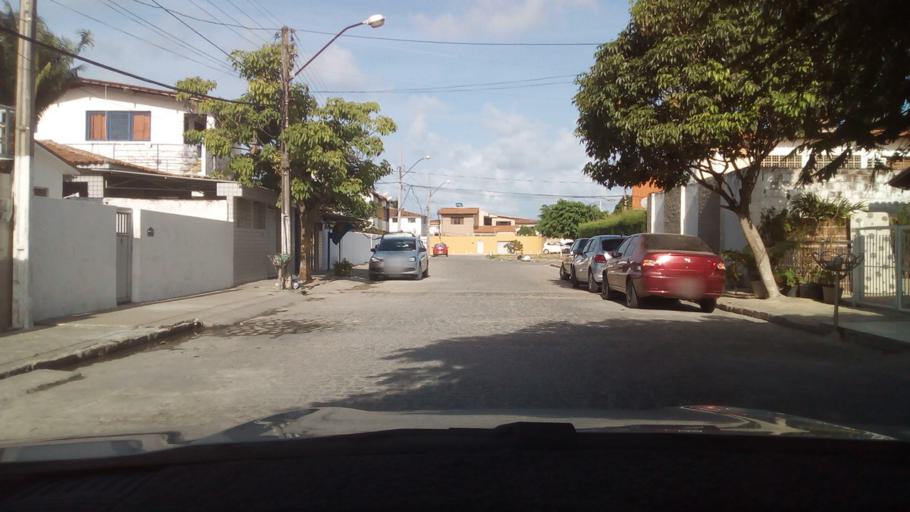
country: BR
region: Paraiba
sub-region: Cabedelo
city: Cabedelo
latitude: -6.9768
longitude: -34.8305
